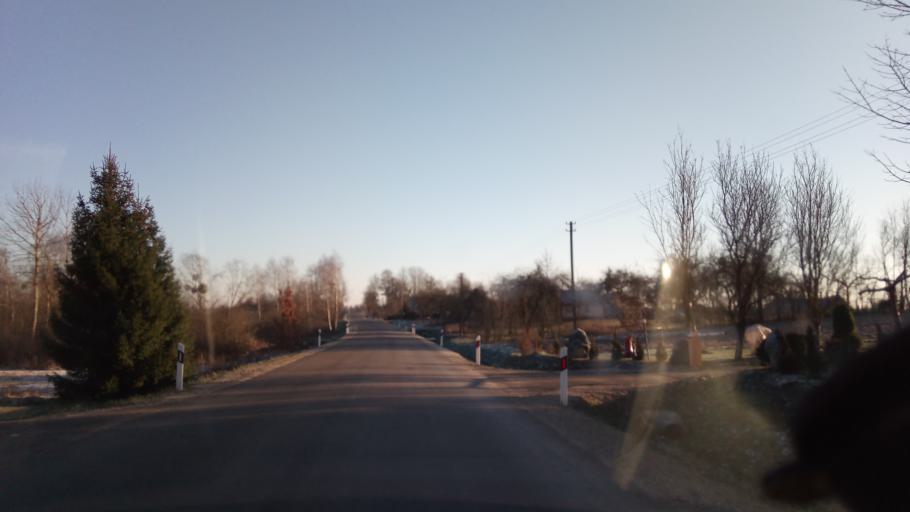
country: LT
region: Alytaus apskritis
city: Druskininkai
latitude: 54.1397
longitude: 23.9709
